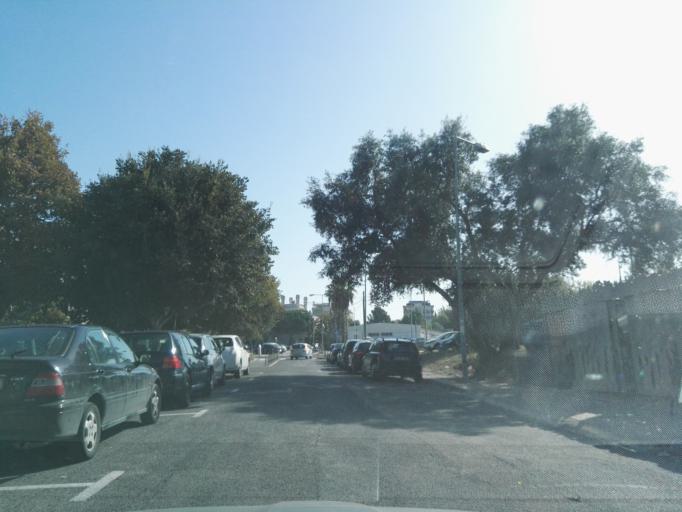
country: PT
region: Lisbon
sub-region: Lisbon
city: Lisbon
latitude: 38.7495
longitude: -9.1557
